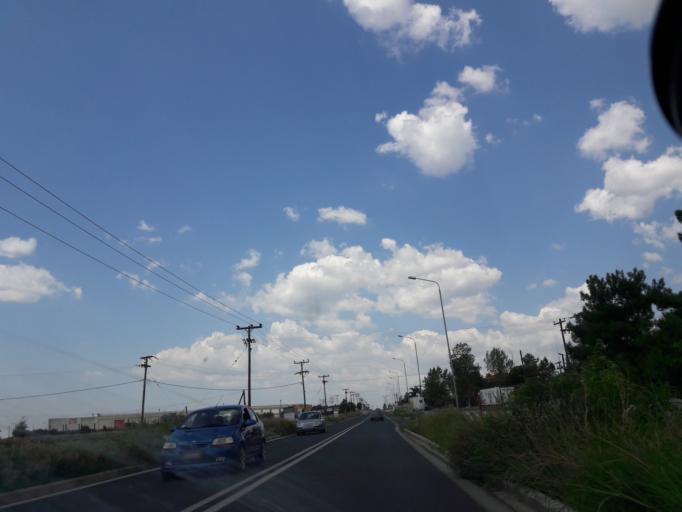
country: GR
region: Central Macedonia
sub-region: Nomos Thessalonikis
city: Thermi
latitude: 40.5281
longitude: 23.0454
